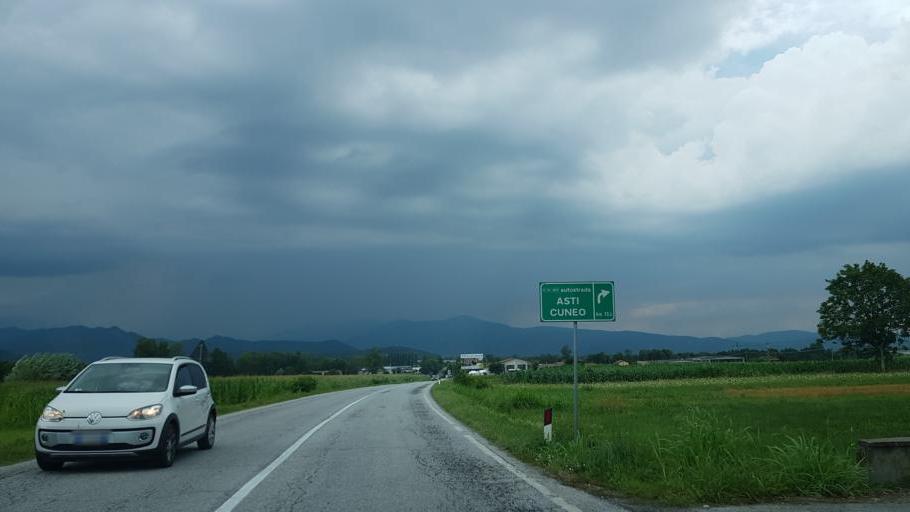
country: IT
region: Piedmont
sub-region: Provincia di Cuneo
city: Cervasca
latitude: 44.3866
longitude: 7.4628
